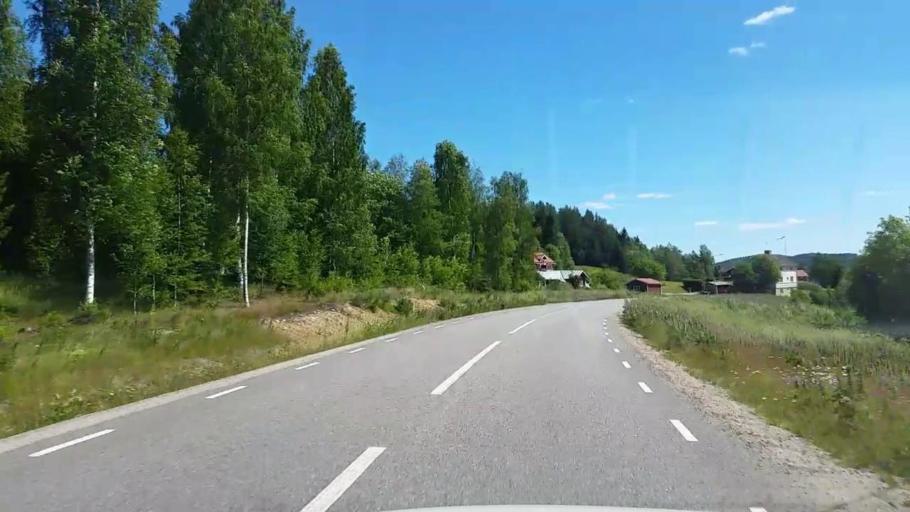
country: SE
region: Gaevleborg
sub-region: Ovanakers Kommun
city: Edsbyn
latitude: 61.4241
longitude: 15.7319
